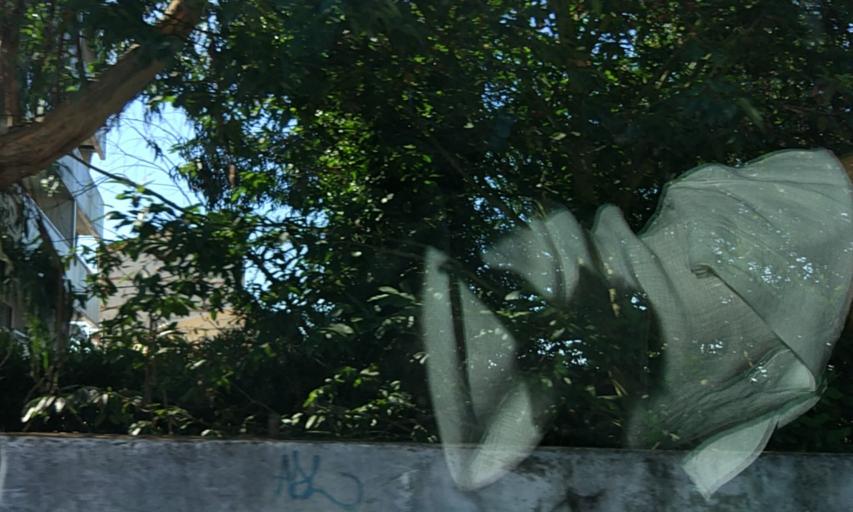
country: PT
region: Porto
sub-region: Gondomar
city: Fanzeres
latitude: 41.1813
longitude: -8.5345
